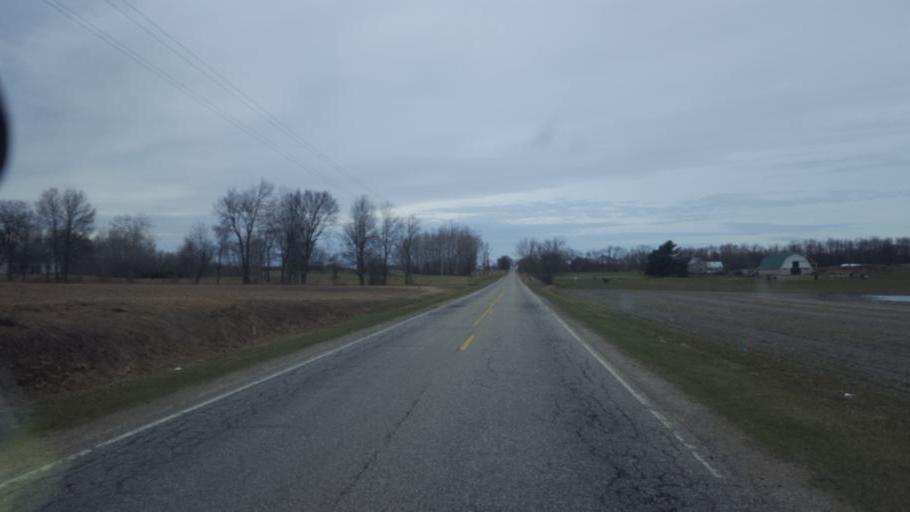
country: US
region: Michigan
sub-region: Montcalm County
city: Edmore
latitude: 43.4574
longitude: -85.0052
